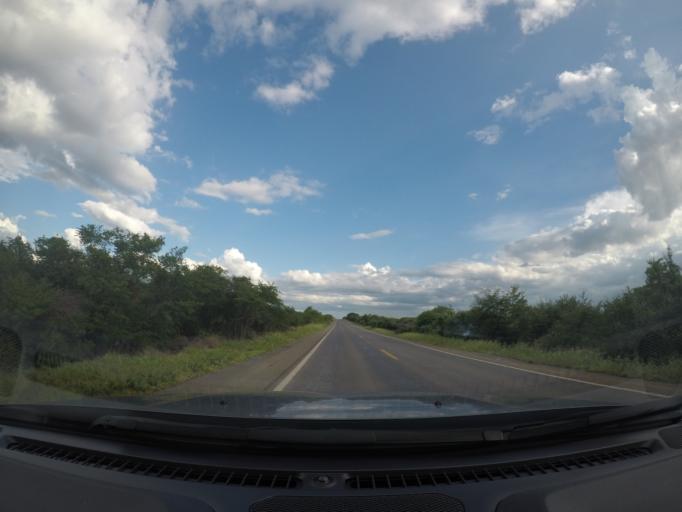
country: BR
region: Bahia
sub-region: Oliveira Dos Brejinhos
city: Beira Rio
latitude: -12.1865
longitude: -42.8281
